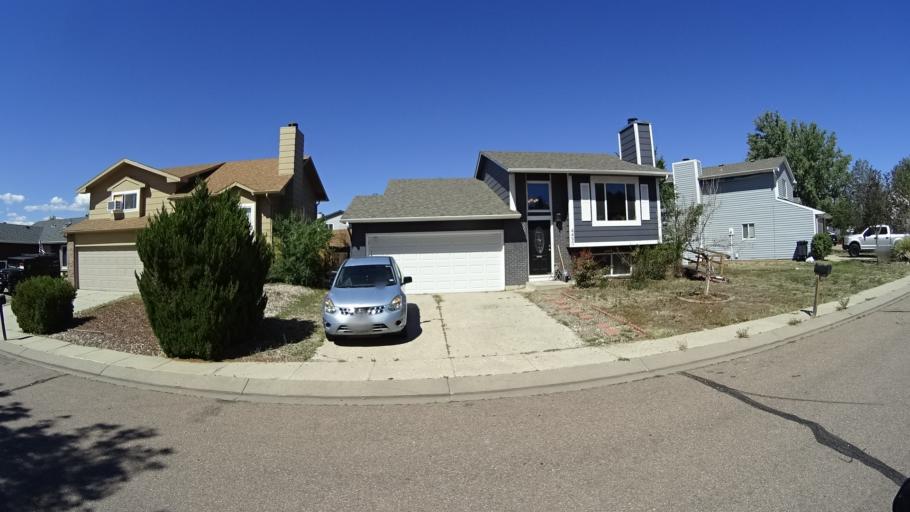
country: US
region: Colorado
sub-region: El Paso County
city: Stratmoor
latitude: 38.7870
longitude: -104.7455
